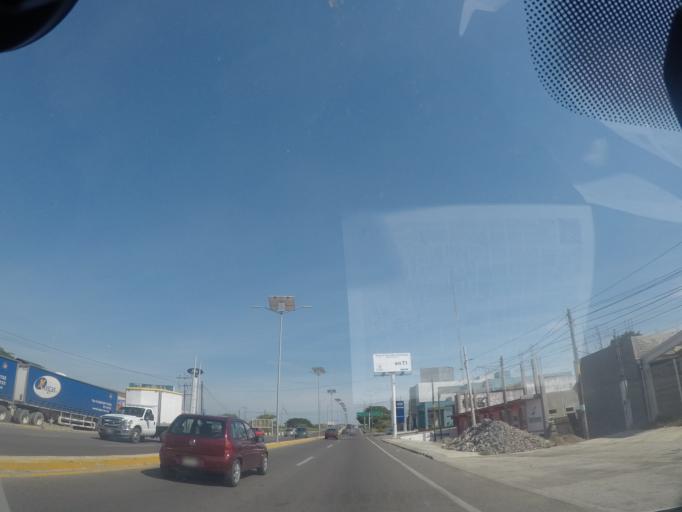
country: MX
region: Oaxaca
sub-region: Santo Domingo Tehuantepec
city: La Noria
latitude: 16.2246
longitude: -95.2094
